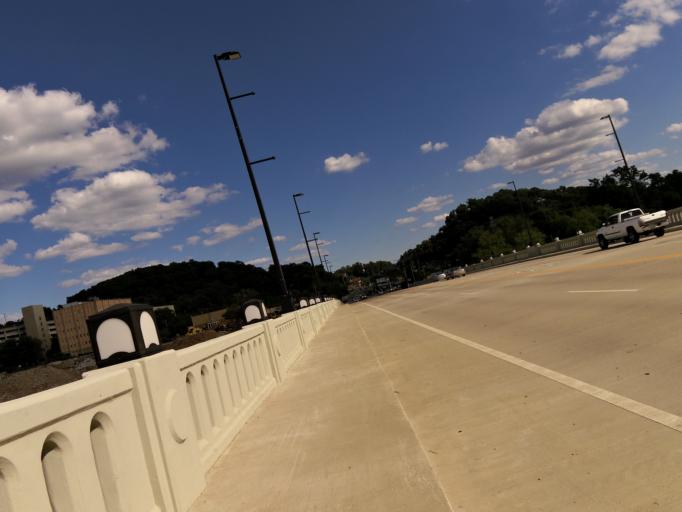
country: US
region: Tennessee
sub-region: Knox County
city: Knoxville
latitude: 35.9564
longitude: -83.9178
